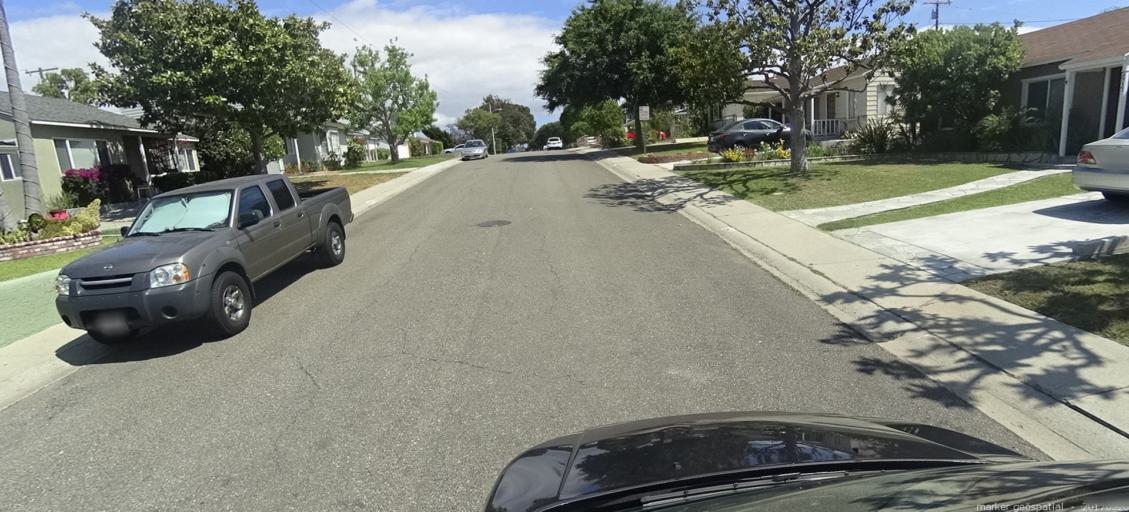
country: US
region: California
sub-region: Los Angeles County
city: Lawndale
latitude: 33.8824
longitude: -118.3639
